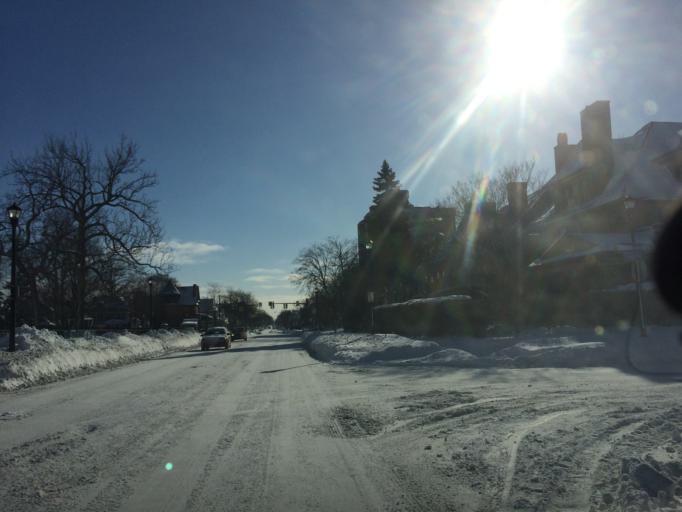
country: US
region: New York
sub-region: Monroe County
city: Rochester
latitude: 43.1569
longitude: -77.5883
